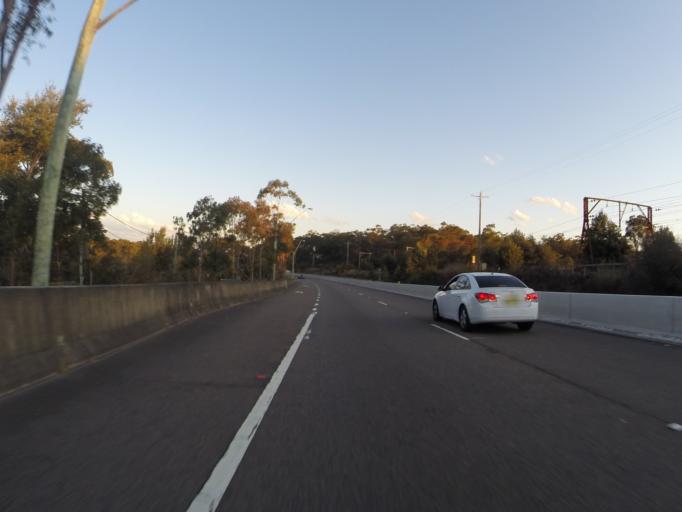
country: AU
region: New South Wales
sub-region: Blue Mountains Municipality
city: Blaxland
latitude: -33.7188
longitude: 150.5932
